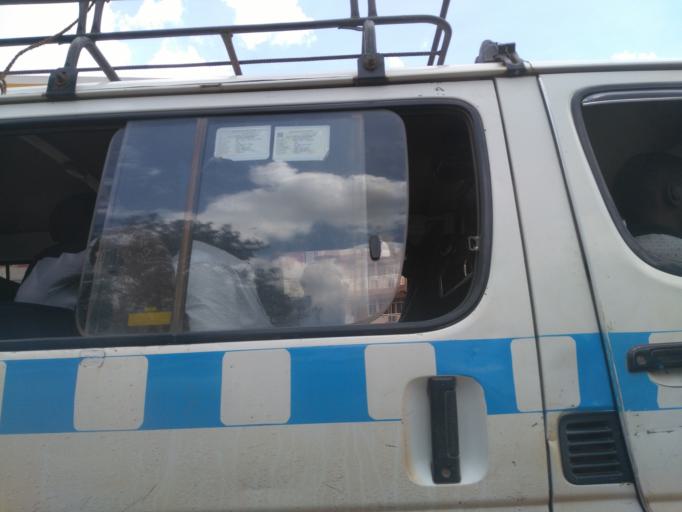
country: UG
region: Central Region
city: Kampala Central Division
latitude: 0.3357
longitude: 32.5727
